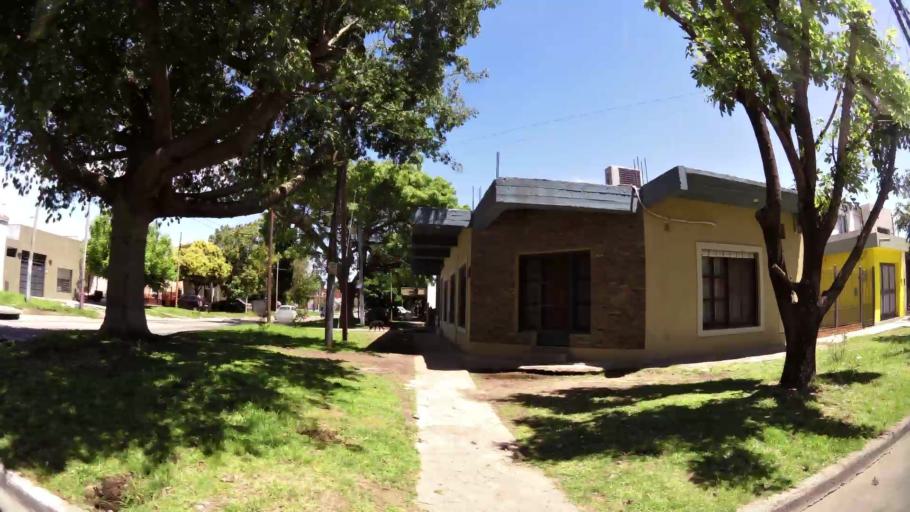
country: AR
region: Buenos Aires
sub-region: Partido de Quilmes
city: Quilmes
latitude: -34.7360
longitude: -58.2864
